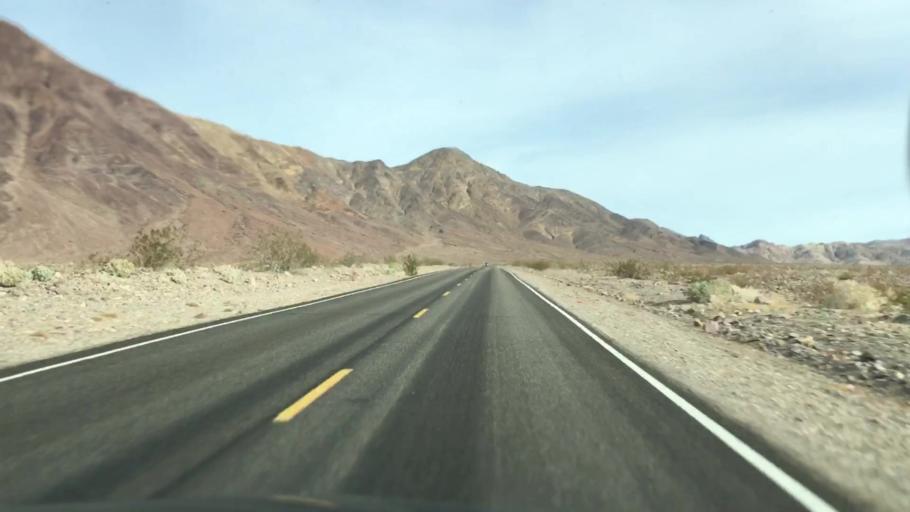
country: US
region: Nevada
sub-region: Nye County
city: Beatty
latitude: 36.6969
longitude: -117.0004
